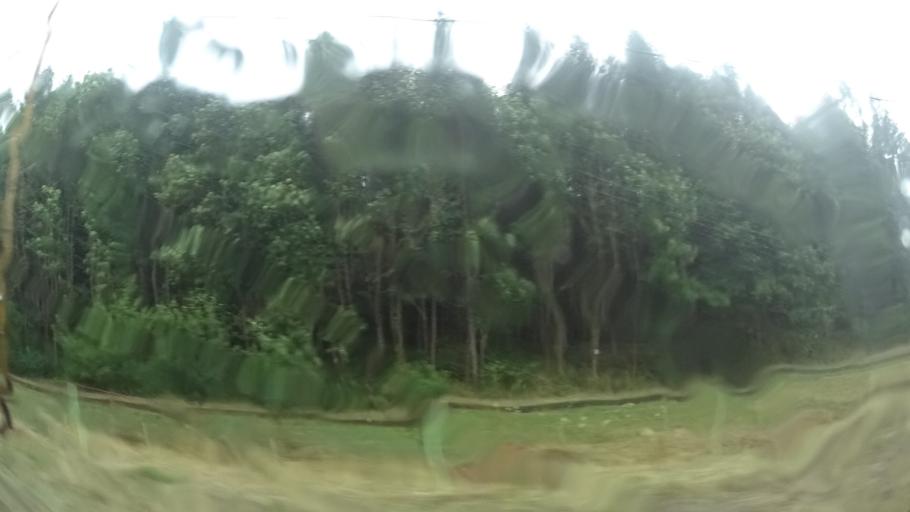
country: DE
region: Thuringia
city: Klettbach
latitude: 50.9049
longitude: 11.1633
